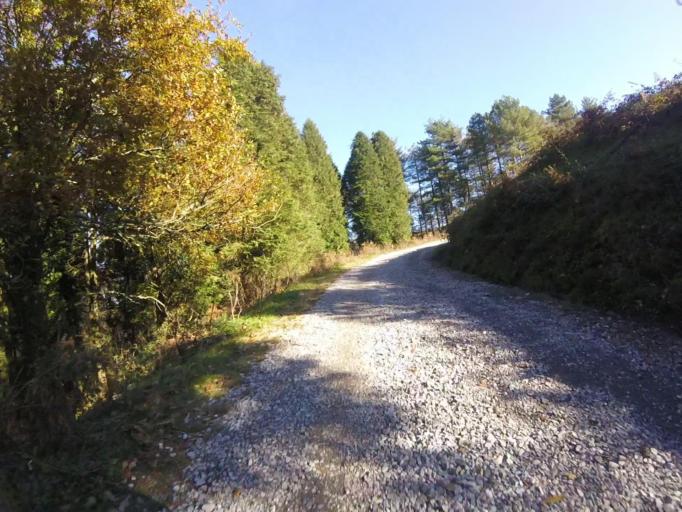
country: ES
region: Navarre
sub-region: Provincia de Navarra
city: Bera
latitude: 43.3125
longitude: -1.6892
